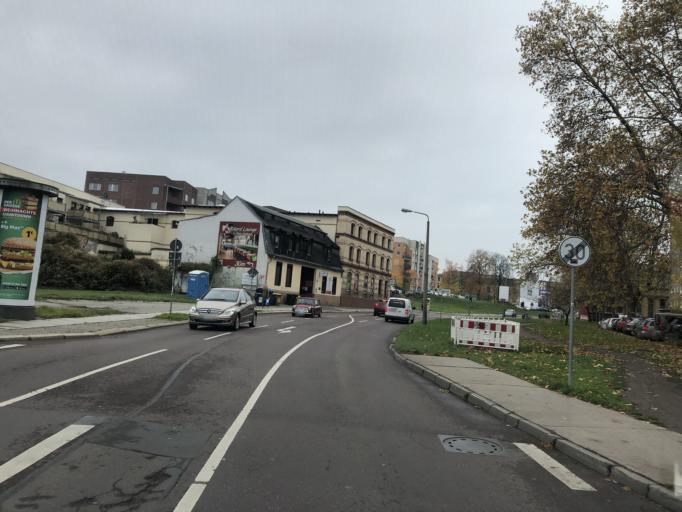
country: DE
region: Saxony-Anhalt
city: Halle (Saale)
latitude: 51.4766
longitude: 11.9621
